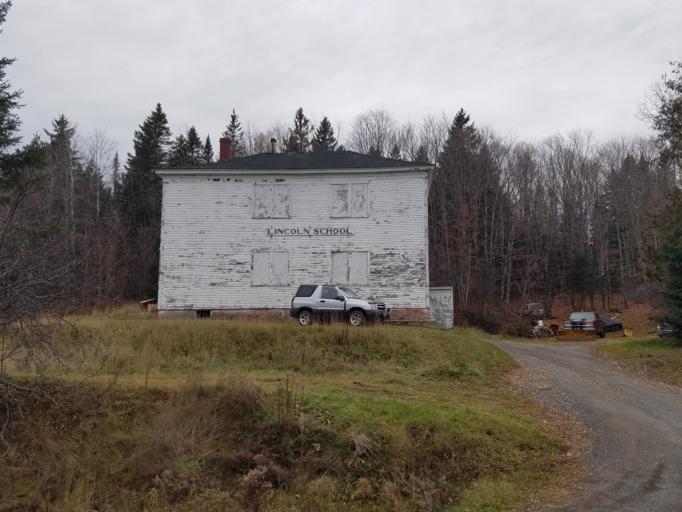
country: US
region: Maine
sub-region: Penobscot County
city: Patten
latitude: 46.1307
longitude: -68.1673
